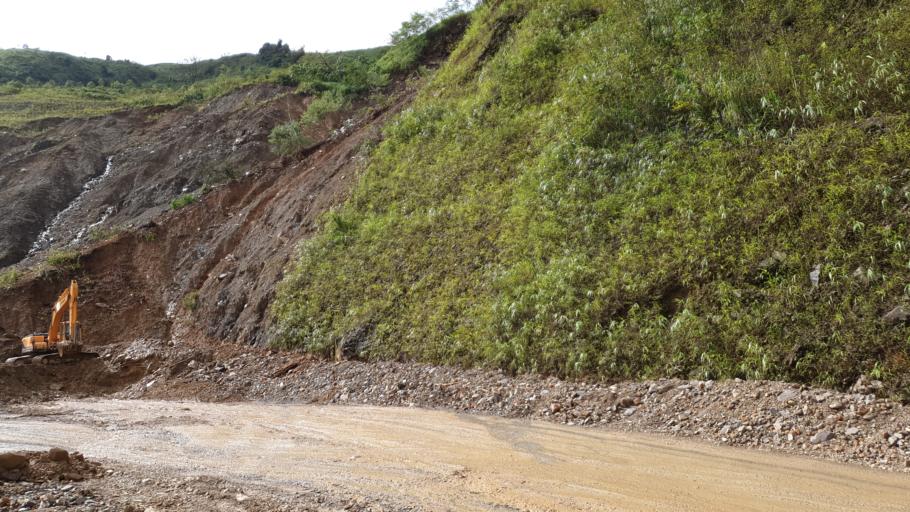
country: LA
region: Vientiane
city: Muang Kasi
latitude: 19.3855
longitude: 102.1473
